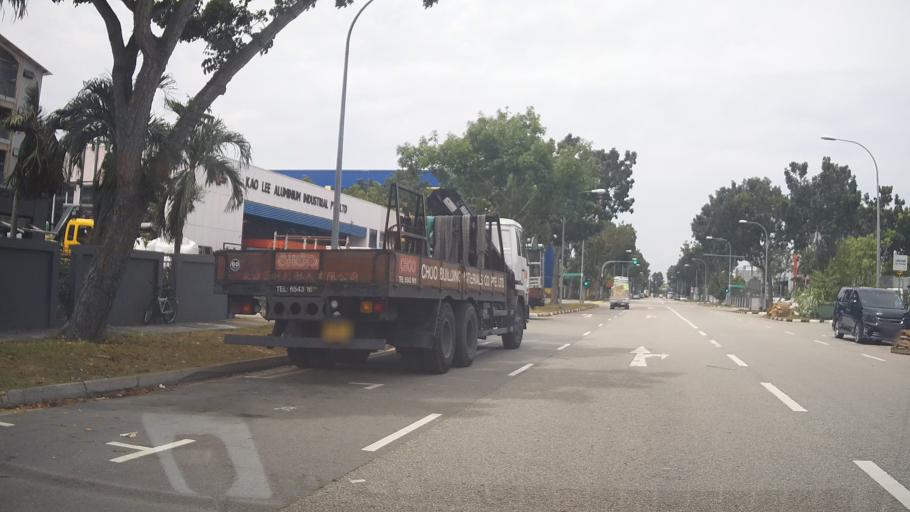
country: SG
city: Singapore
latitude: 1.3348
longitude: 103.9694
